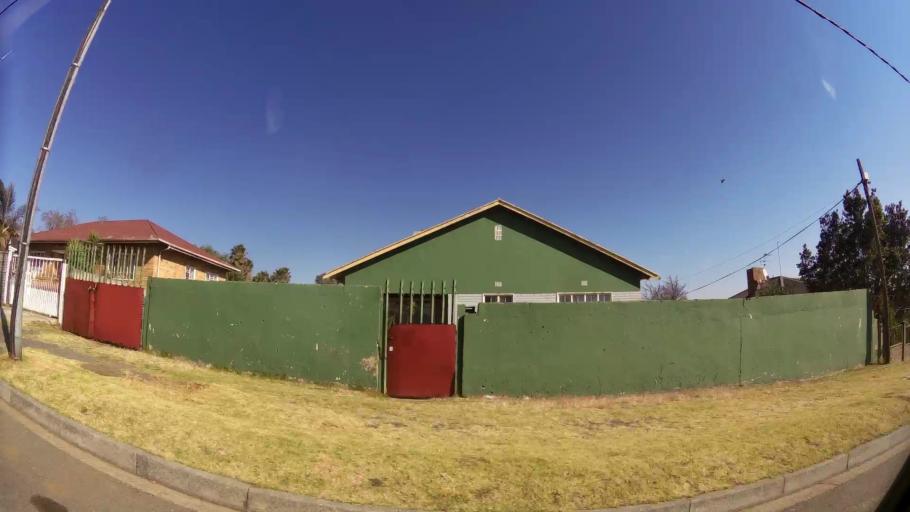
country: ZA
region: Gauteng
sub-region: City of Johannesburg Metropolitan Municipality
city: Johannesburg
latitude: -26.2393
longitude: 28.0932
